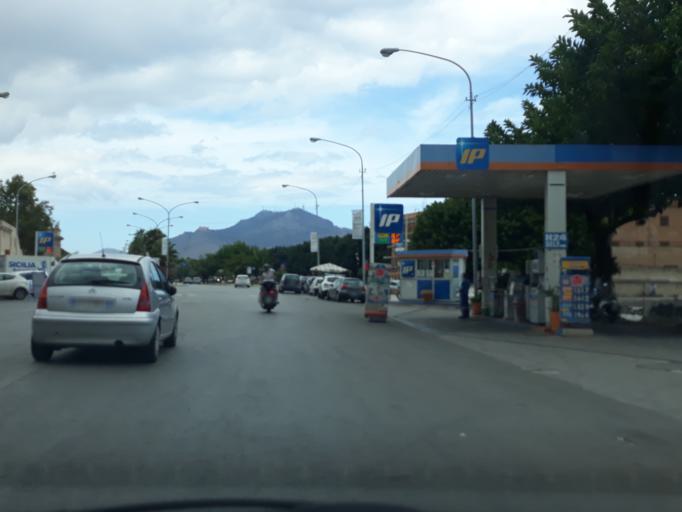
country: IT
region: Sicily
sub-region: Palermo
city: Ciaculli
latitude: 38.1123
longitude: 13.3783
